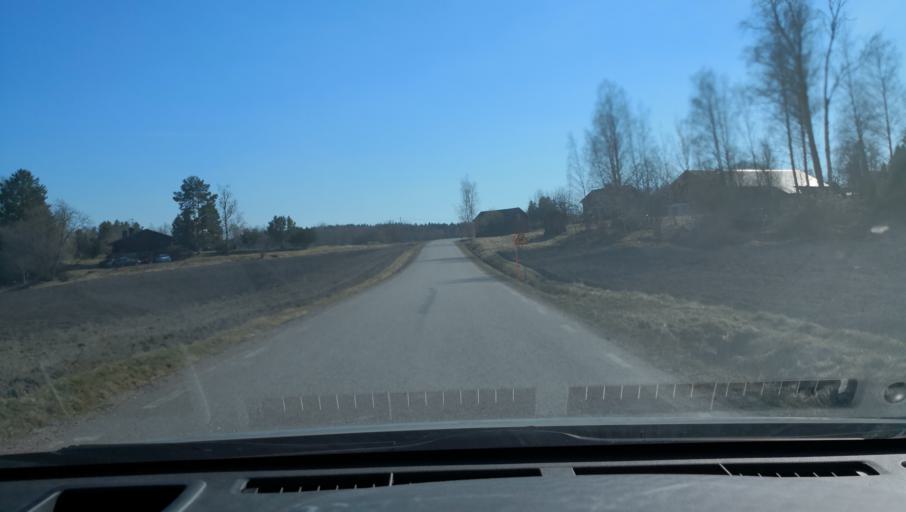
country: SE
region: Vaestmanland
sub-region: Sala Kommun
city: Sala
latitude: 60.0797
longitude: 16.4959
